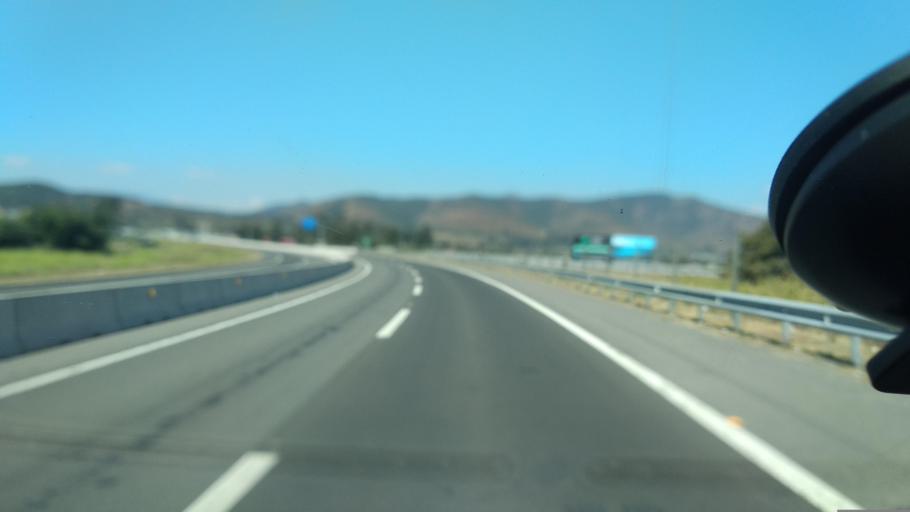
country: CL
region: Valparaiso
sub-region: Provincia de Marga Marga
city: Limache
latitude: -32.9811
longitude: -71.3093
